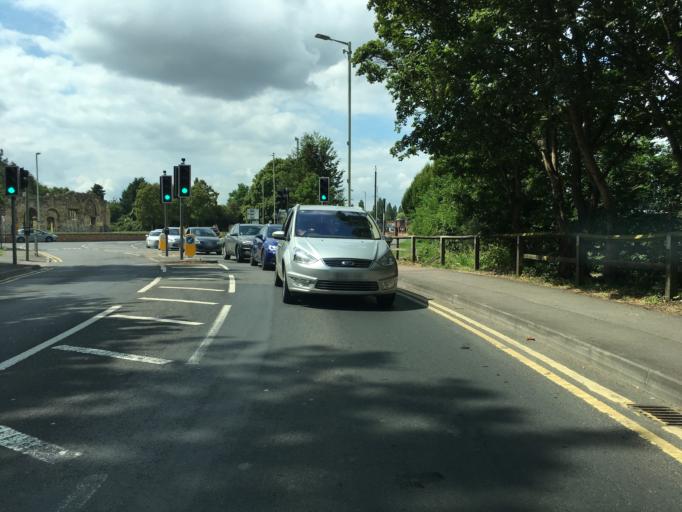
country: GB
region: England
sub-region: Gloucestershire
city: Gloucester
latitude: 51.8697
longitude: -2.2462
